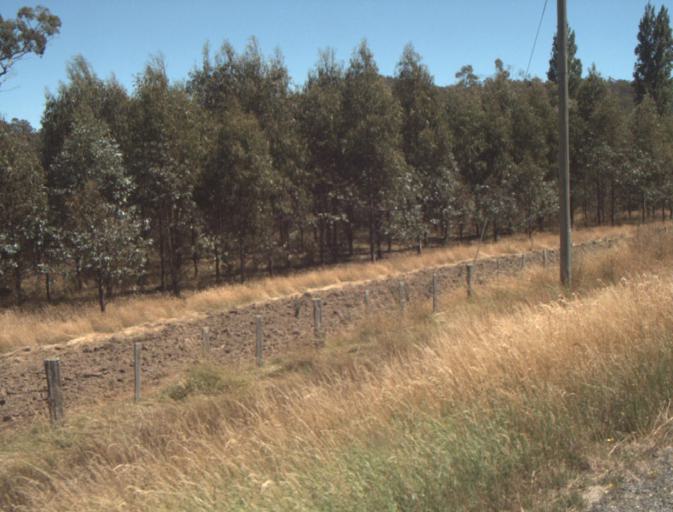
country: AU
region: Tasmania
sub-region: Launceston
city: Newstead
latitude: -41.3796
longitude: 147.3112
